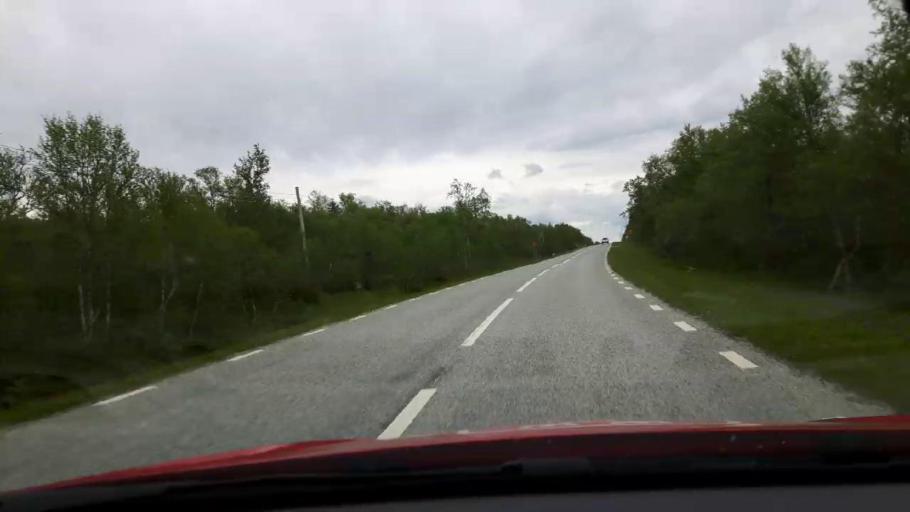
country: NO
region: Sor-Trondelag
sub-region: Tydal
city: Aas
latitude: 62.6080
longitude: 12.1609
